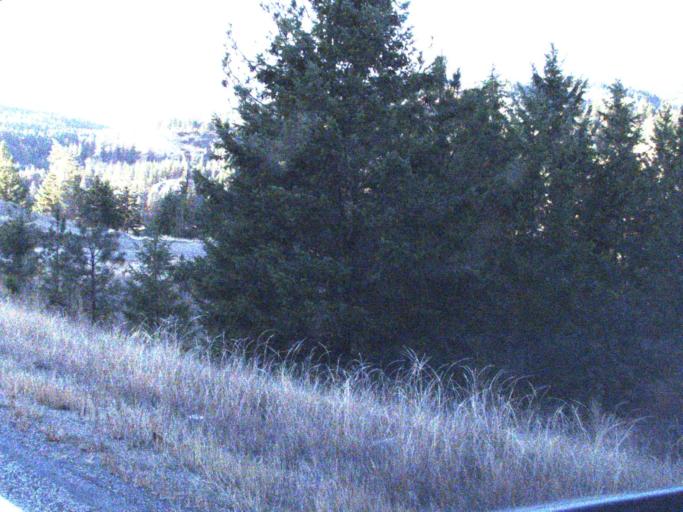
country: US
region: Washington
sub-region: Stevens County
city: Kettle Falls
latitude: 48.8148
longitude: -117.9695
